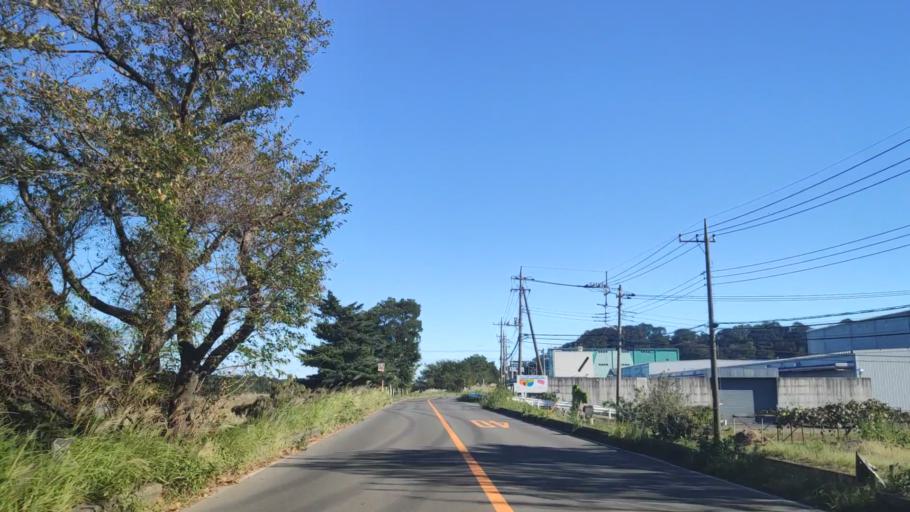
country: JP
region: Kanagawa
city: Zama
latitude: 35.5358
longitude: 139.3361
